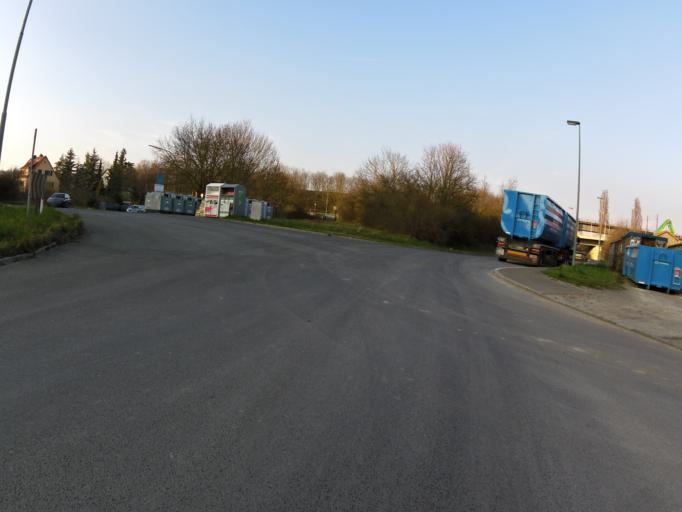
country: DE
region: Bavaria
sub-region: Regierungsbezirk Unterfranken
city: Kitzingen
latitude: 49.7247
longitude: 10.1607
